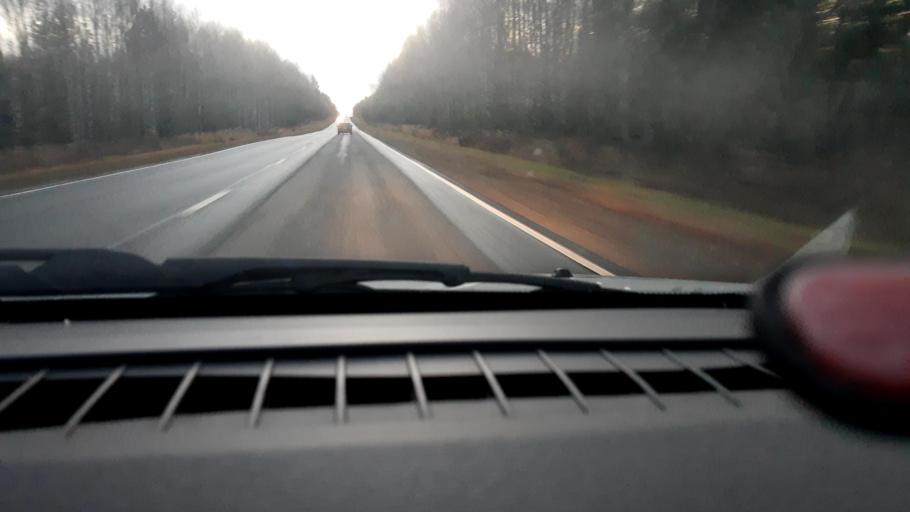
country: RU
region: Nizjnij Novgorod
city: Vladimirskoye
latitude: 56.9529
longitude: 45.0911
